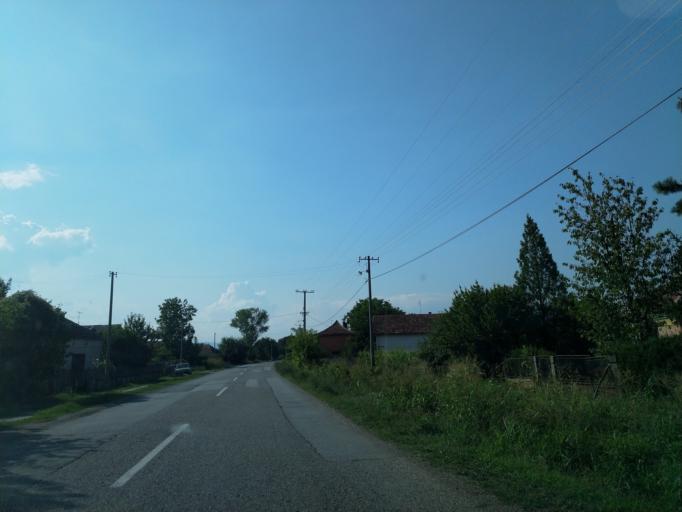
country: RS
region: Central Serbia
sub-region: Rasinski Okrug
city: Cicevac
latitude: 43.7545
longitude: 21.4368
